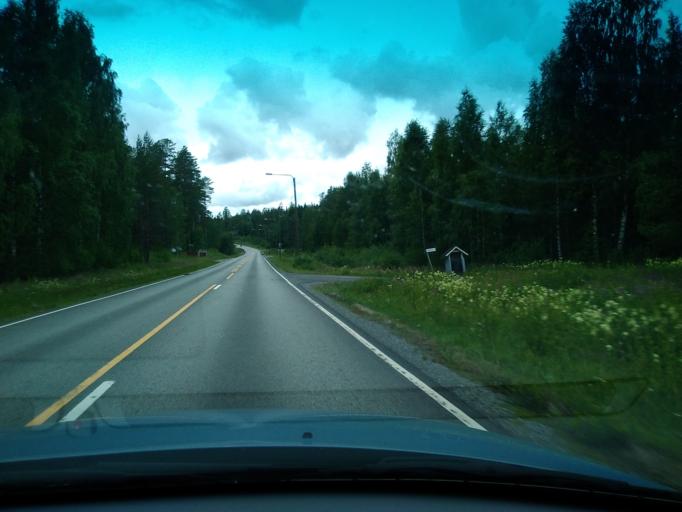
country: FI
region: Central Finland
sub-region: Saarijaervi-Viitasaari
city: Pylkoenmaeki
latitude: 62.6409
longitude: 24.8464
